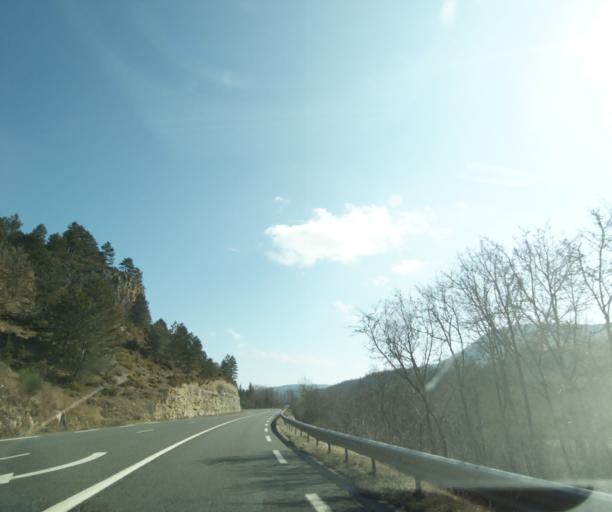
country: FR
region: Languedoc-Roussillon
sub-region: Departement de la Lozere
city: Chirac
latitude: 44.4857
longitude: 3.2912
